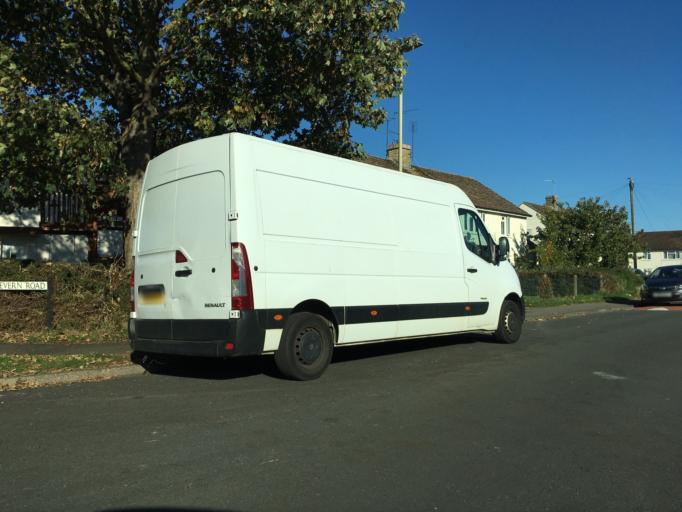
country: GB
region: England
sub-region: Gloucestershire
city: Stonehouse
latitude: 51.7489
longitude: -2.2909
